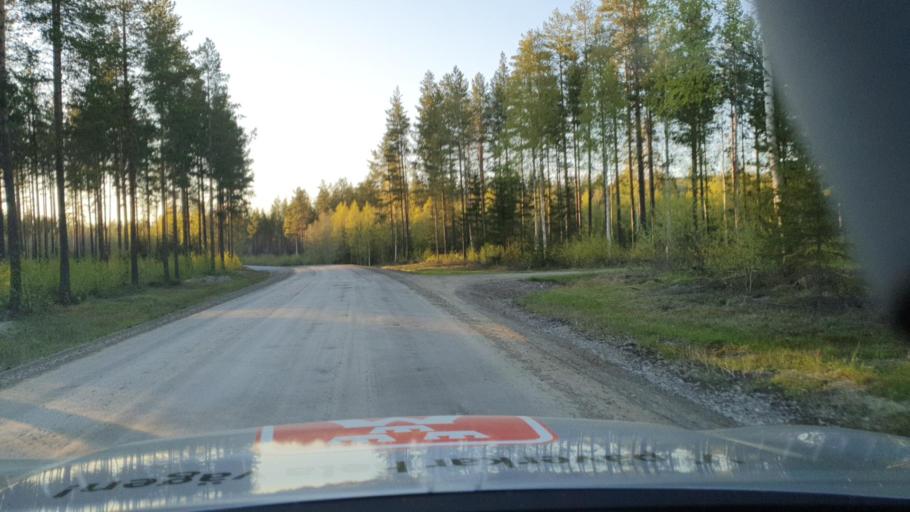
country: SE
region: Vaesternorrland
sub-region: OErnskoeldsviks Kommun
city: Bjasta
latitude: 63.4559
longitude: 18.4158
